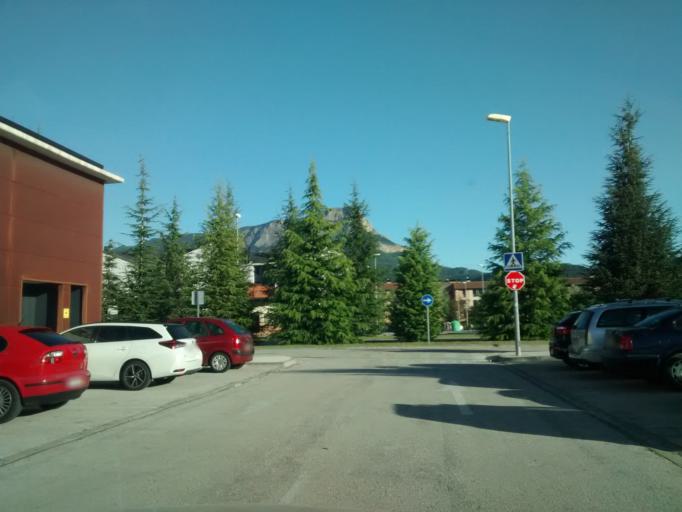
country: ES
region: Aragon
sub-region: Provincia de Huesca
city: Jaca
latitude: 42.5652
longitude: -0.5649
